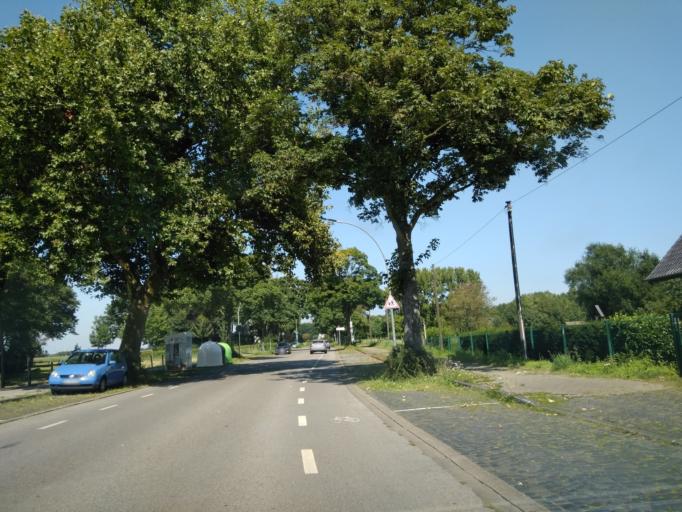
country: DE
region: North Rhine-Westphalia
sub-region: Regierungsbezirk Munster
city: Gelsenkirchen
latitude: 51.5488
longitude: 7.0613
